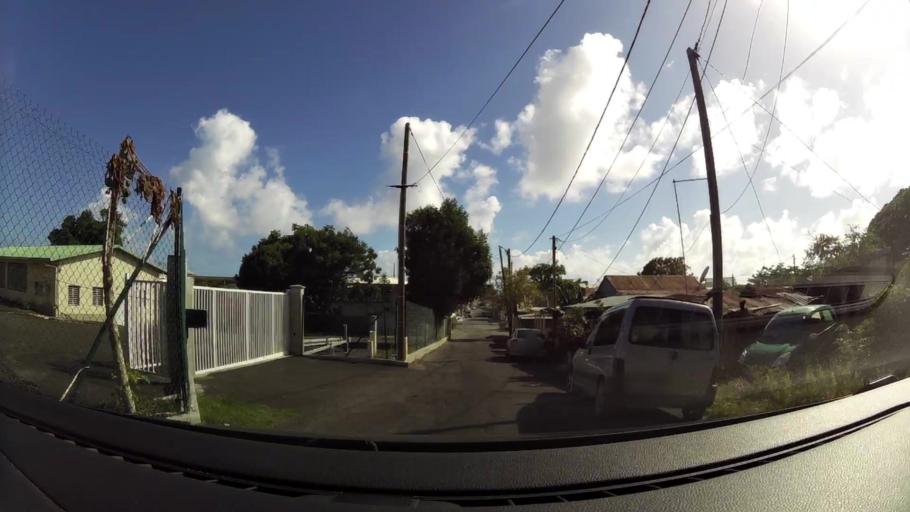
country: GP
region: Guadeloupe
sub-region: Guadeloupe
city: Sainte-Anne
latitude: 16.2273
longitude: -61.3835
